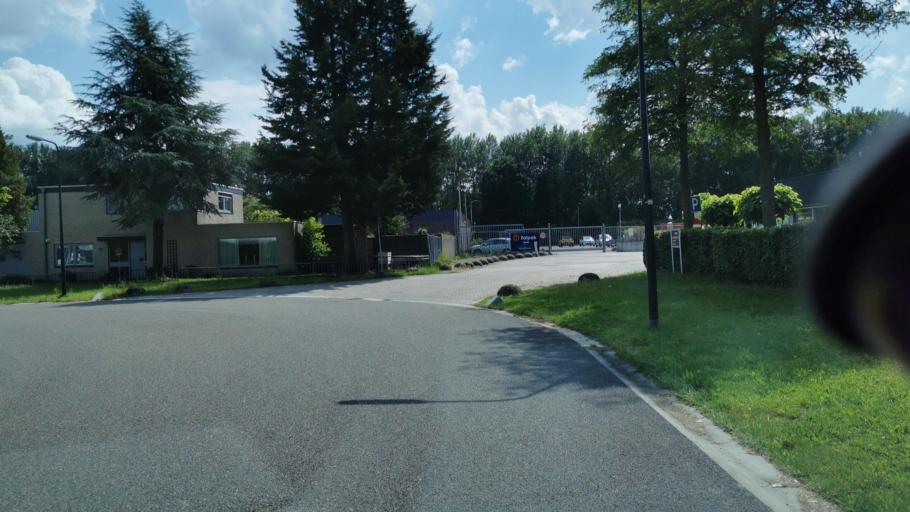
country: NL
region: Overijssel
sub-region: Gemeente Enschede
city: Enschede
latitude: 52.2228
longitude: 6.9488
